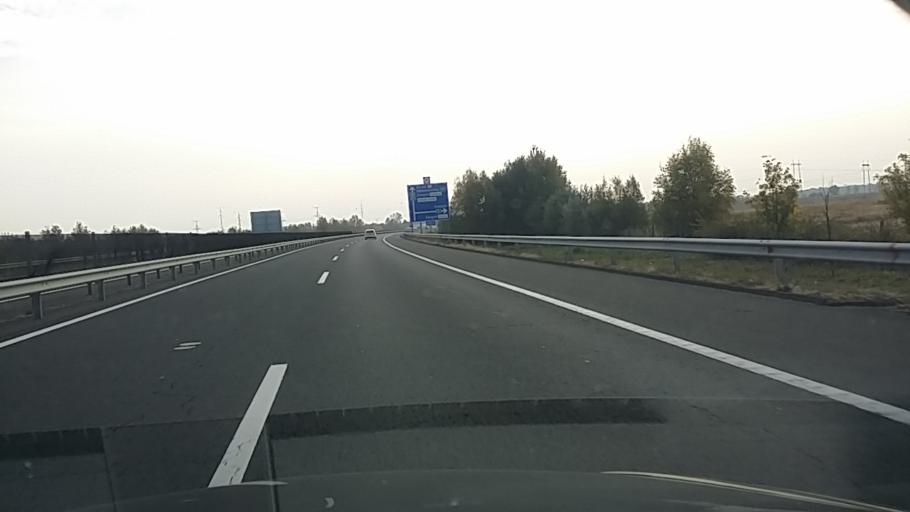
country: HU
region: Csongrad
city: Szatymaz
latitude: 46.2978
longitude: 20.0601
